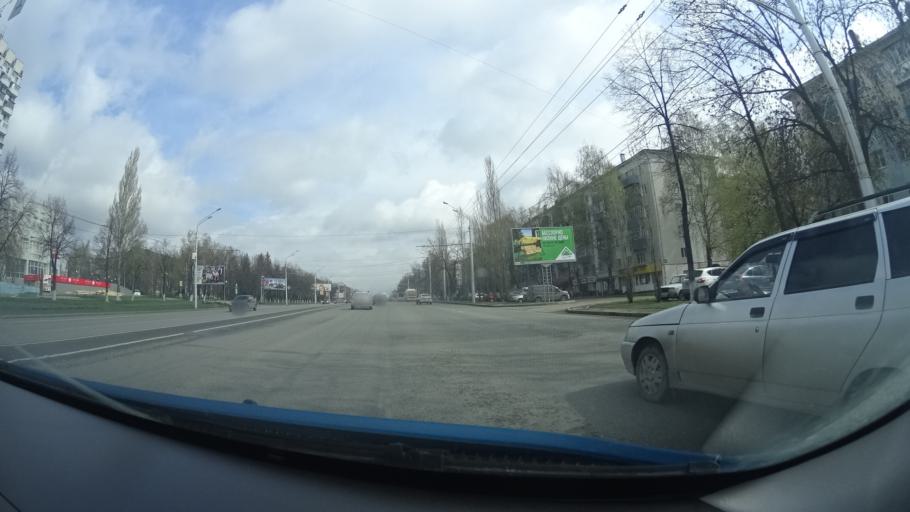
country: RU
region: Bashkortostan
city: Ufa
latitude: 54.7632
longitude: 56.0146
